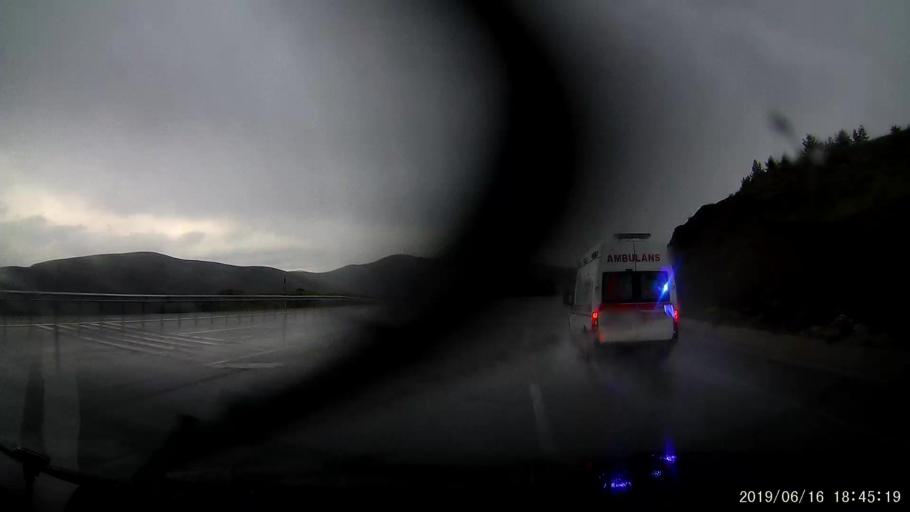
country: TR
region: Erzincan
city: Doganbeyli
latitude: 39.8703
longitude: 39.0592
